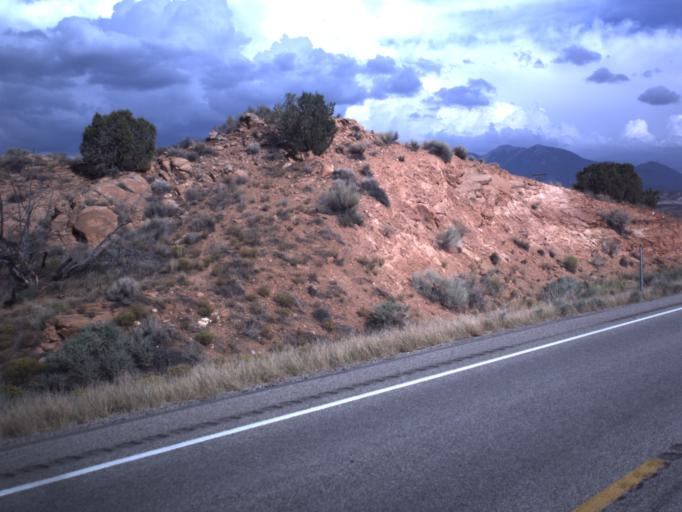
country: US
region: Utah
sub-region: Grand County
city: Moab
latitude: 38.4680
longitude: -109.4512
